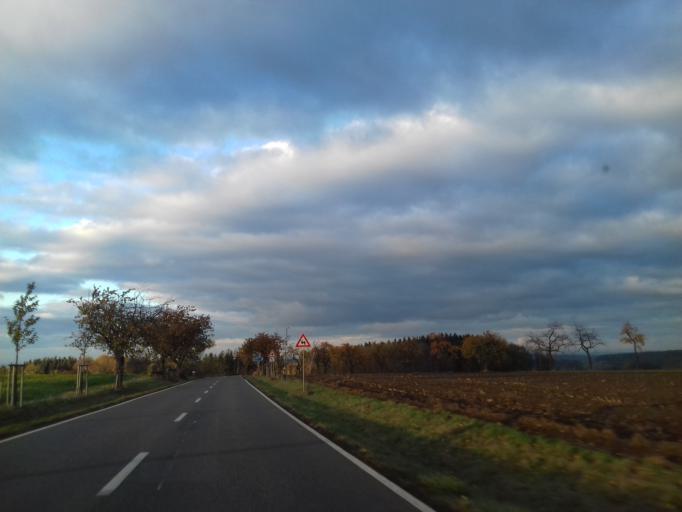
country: CZ
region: Pardubicky
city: Krouna
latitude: 49.8109
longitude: 16.0427
